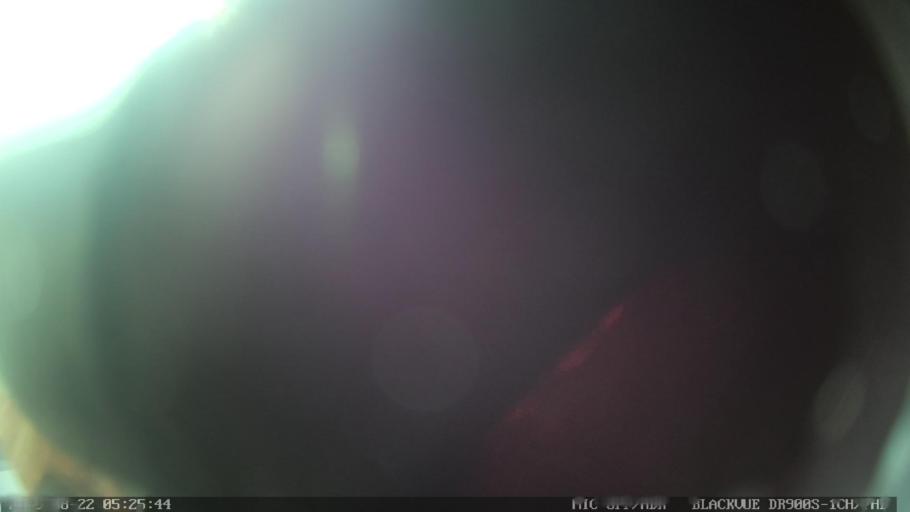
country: PT
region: Castelo Branco
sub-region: Idanha-A-Nova
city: Idanha-a-Nova
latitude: 39.9221
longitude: -7.2379
